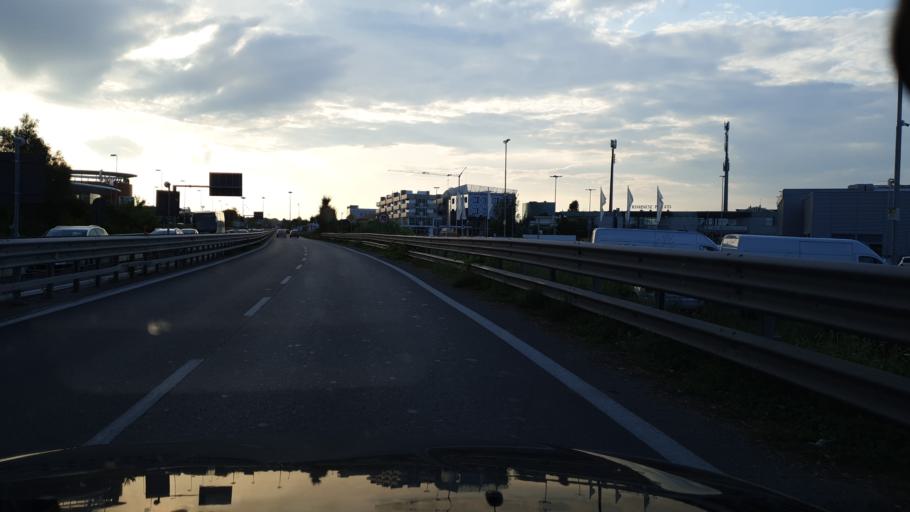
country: IT
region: Emilia-Romagna
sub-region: Provincia di Rimini
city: Rivazzurra
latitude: 44.0412
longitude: 12.5894
